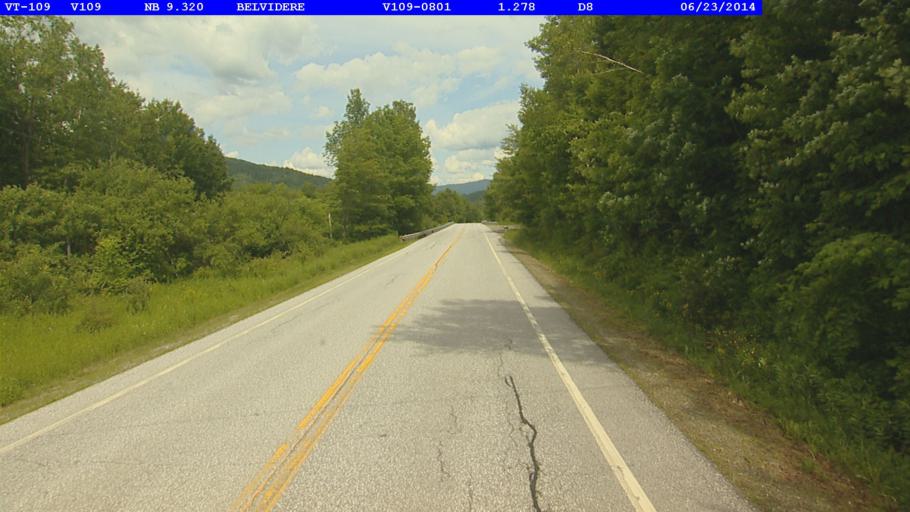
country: US
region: Vermont
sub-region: Lamoille County
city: Johnson
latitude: 44.7439
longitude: -72.7210
